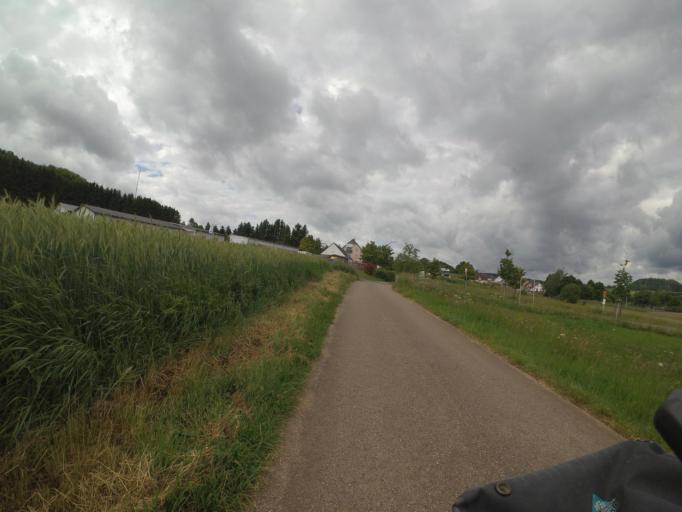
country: DE
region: Rheinland-Pfalz
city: Hinterweiler
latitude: 50.2334
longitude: 6.7510
